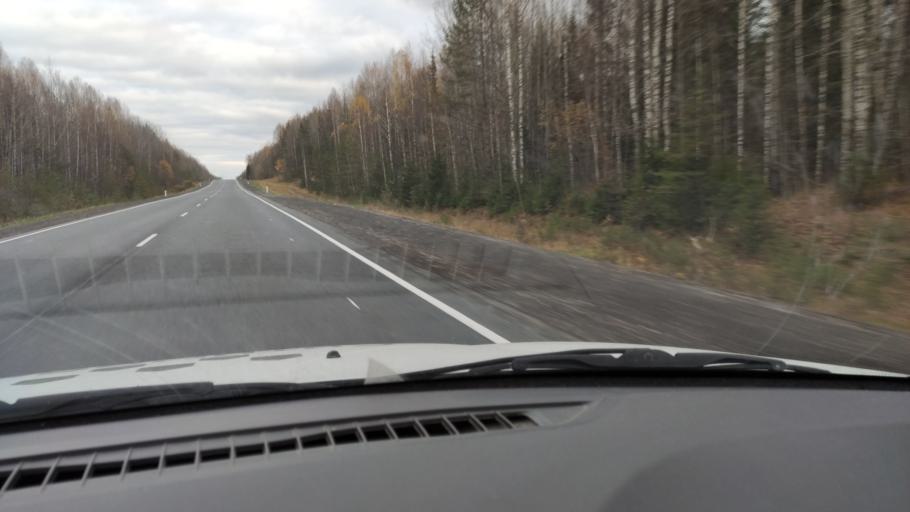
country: RU
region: Kirov
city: Chernaya Kholunitsa
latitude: 58.8826
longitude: 51.4216
